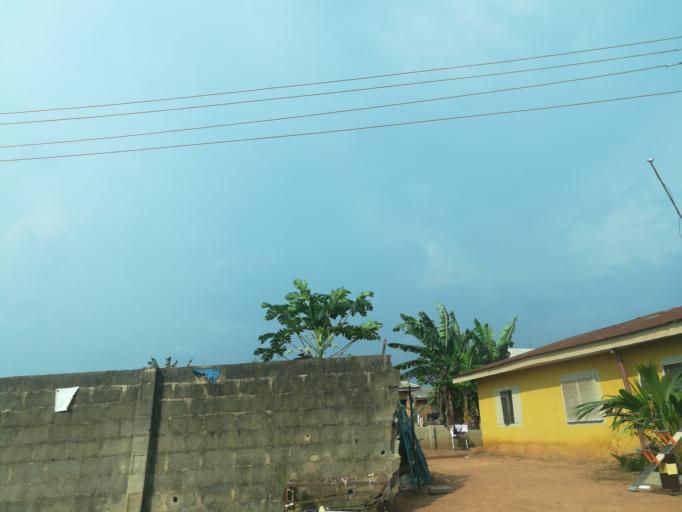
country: NG
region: Lagos
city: Ikorodu
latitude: 6.6638
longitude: 3.6667
